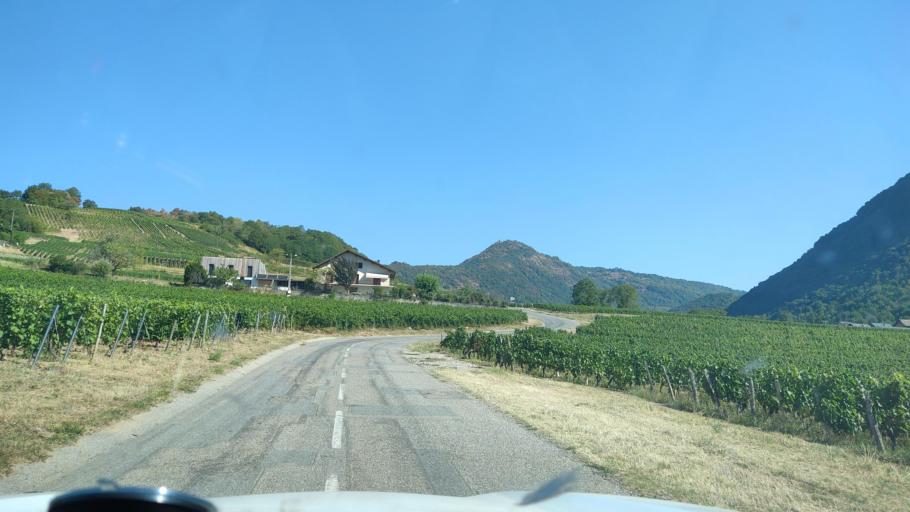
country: FR
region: Rhone-Alpes
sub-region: Departement de la Savoie
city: Les Marches
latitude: 45.5290
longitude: 6.0067
